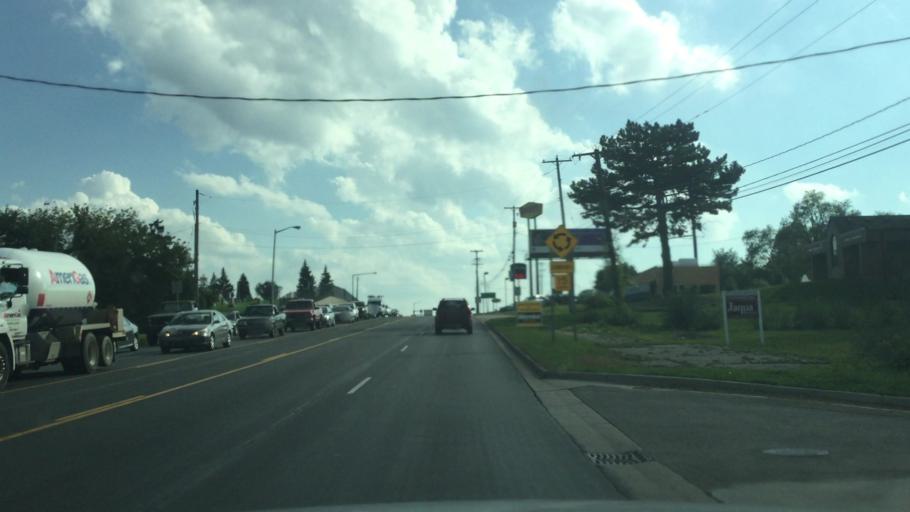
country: US
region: Michigan
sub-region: Kalamazoo County
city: Eastwood
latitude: 42.2647
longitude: -85.5309
